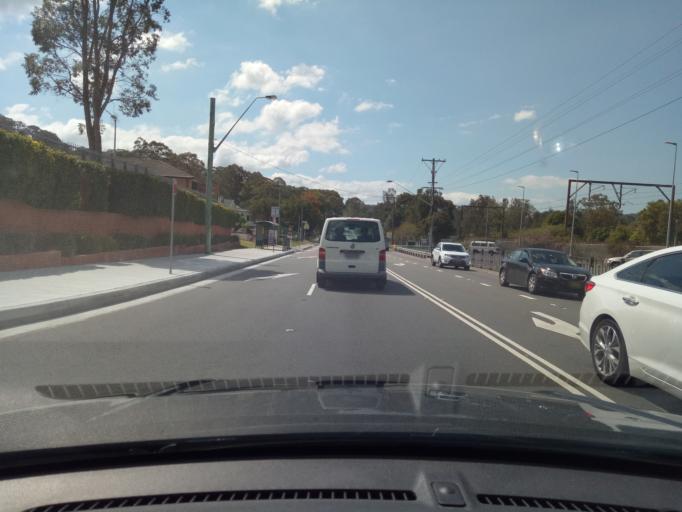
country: AU
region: New South Wales
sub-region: Gosford Shire
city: Point Clare
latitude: -33.4459
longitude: 151.3282
